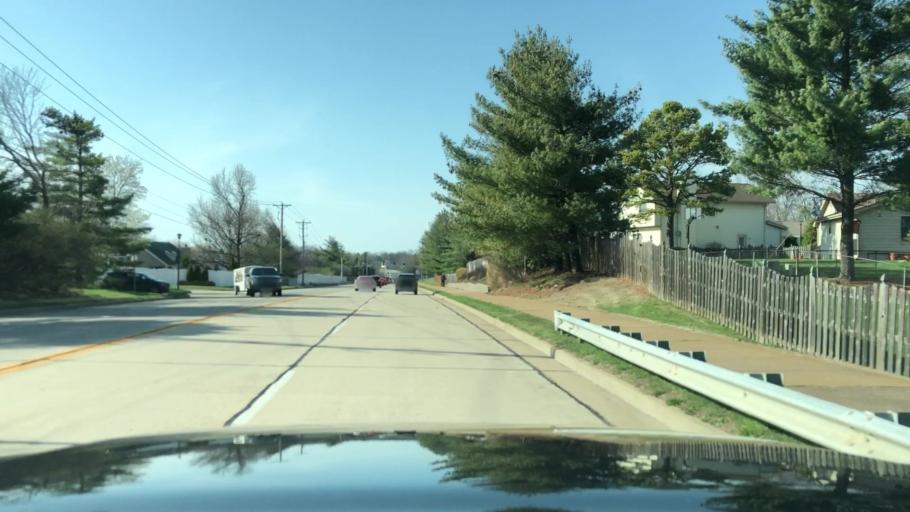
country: US
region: Missouri
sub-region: Saint Charles County
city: Saint Charles
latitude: 38.7746
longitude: -90.5515
